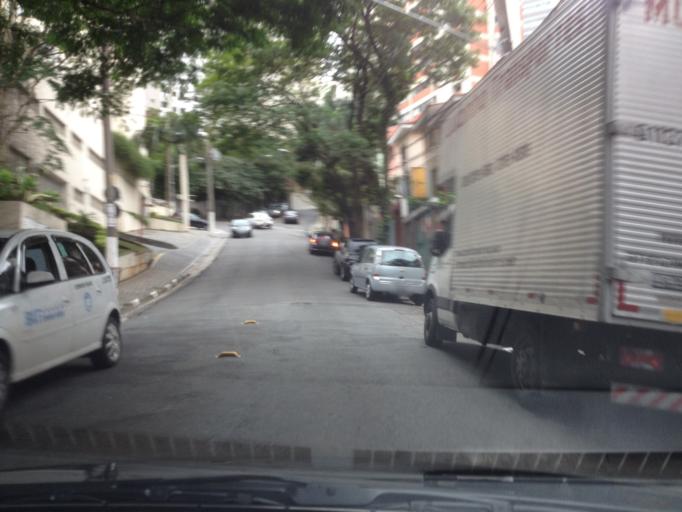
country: BR
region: Sao Paulo
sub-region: Sao Paulo
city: Sao Paulo
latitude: -23.5474
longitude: -46.6944
